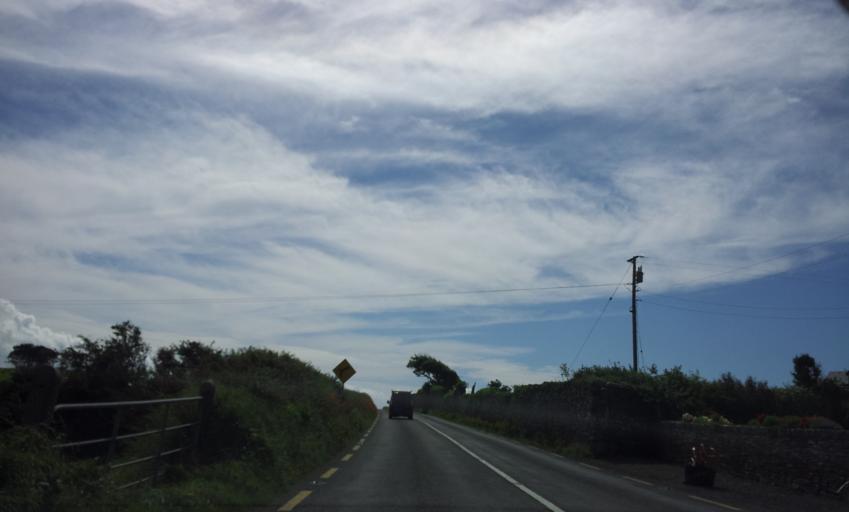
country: IE
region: Munster
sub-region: Ciarrai
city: Dingle
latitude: 52.1323
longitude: -10.2443
